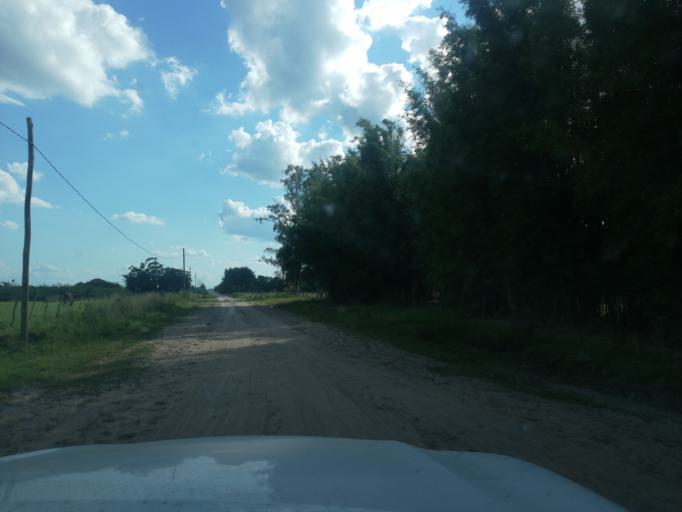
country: AR
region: Corrientes
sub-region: Departamento de San Miguel
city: San Miguel
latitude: -27.9927
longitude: -57.5760
